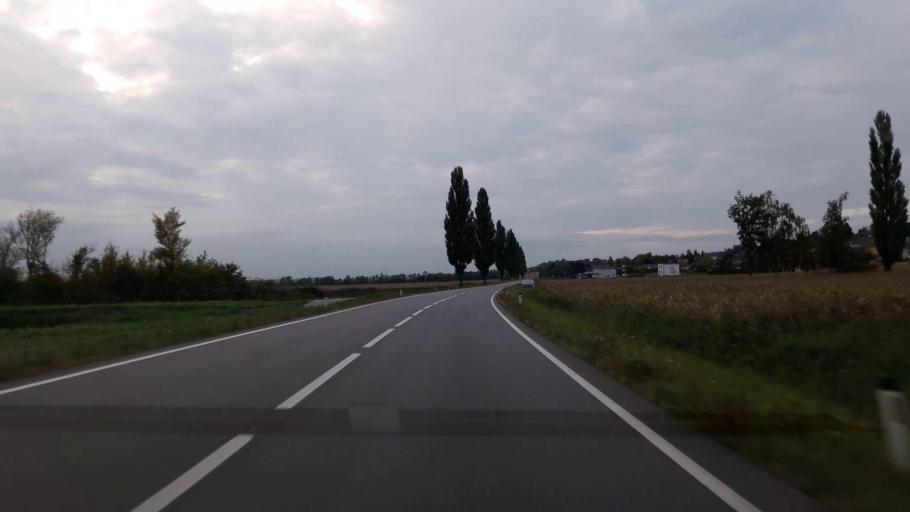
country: AT
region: Lower Austria
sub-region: Politischer Bezirk Bruck an der Leitha
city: Trautmannsdorf an der Leitha
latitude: 48.0533
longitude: 16.6372
